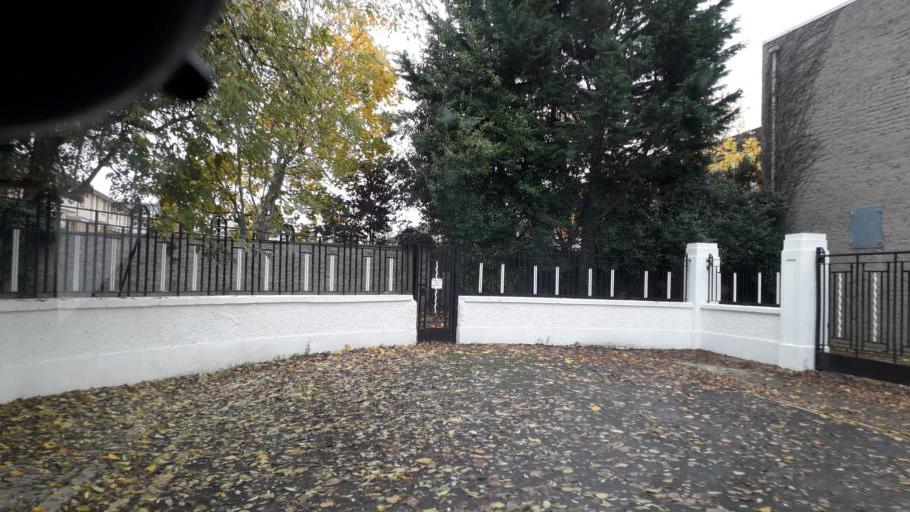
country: IE
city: Milltown
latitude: 53.3151
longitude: -6.2514
